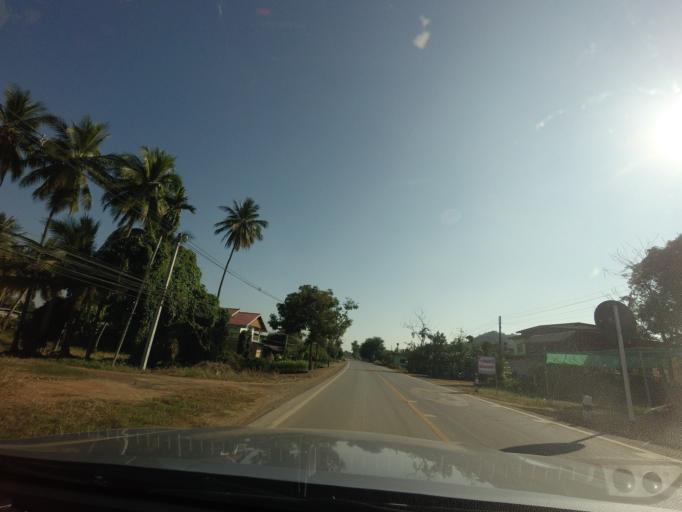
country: TH
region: Sukhothai
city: Sawankhalok
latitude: 17.4138
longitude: 99.7988
